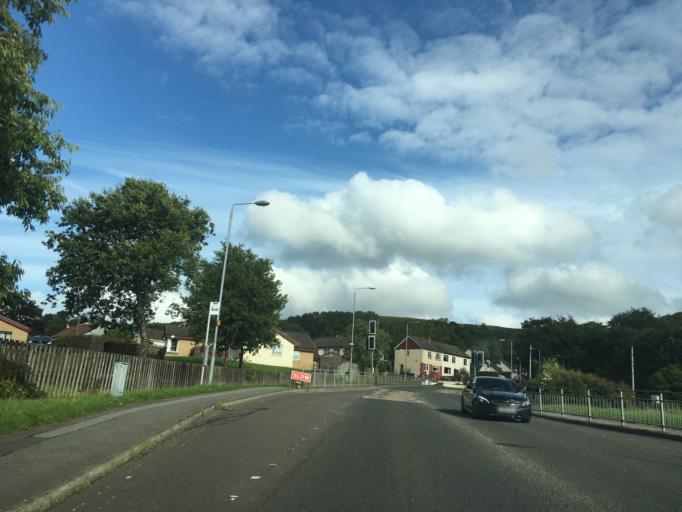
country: GB
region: Scotland
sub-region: Argyll and Bute
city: Oban
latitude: 56.4001
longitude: -5.4716
